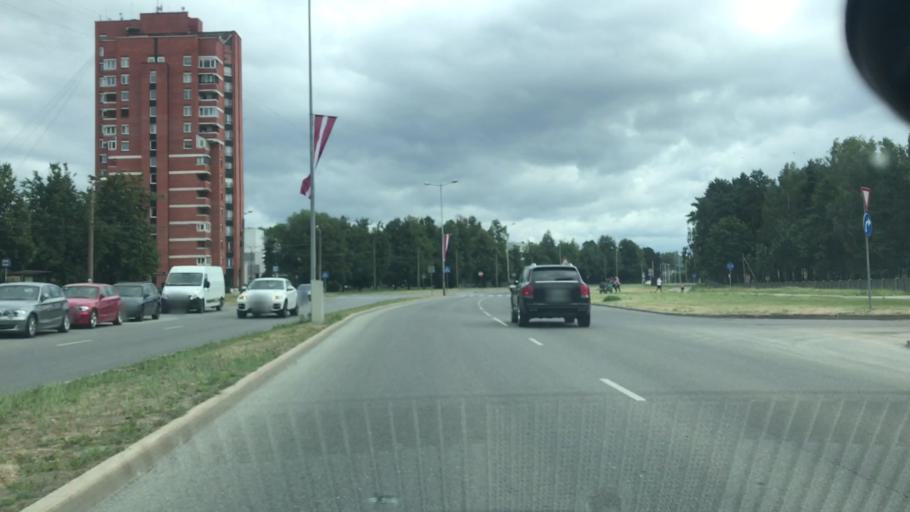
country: LV
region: Marupe
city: Marupe
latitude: 56.9600
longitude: 24.0190
